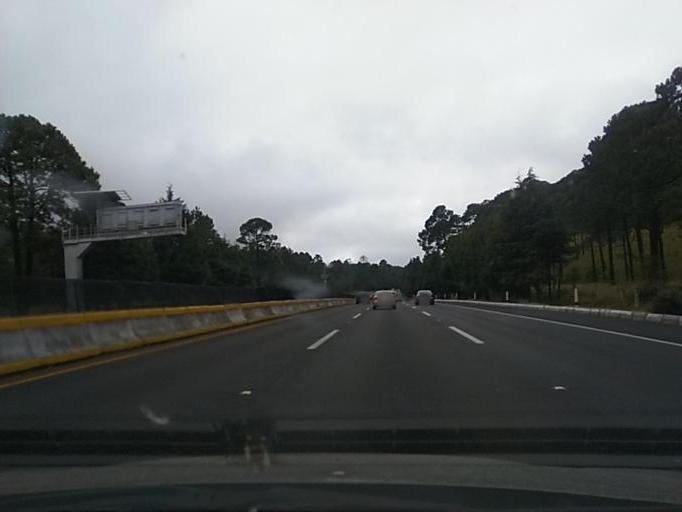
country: MX
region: Morelos
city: Tres Marias
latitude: 19.1119
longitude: -99.1844
